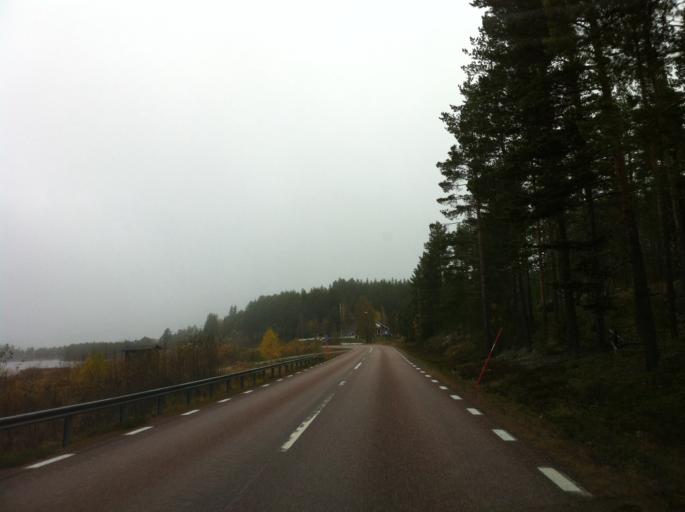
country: NO
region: Hedmark
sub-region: Trysil
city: Innbygda
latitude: 61.8523
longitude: 12.7494
